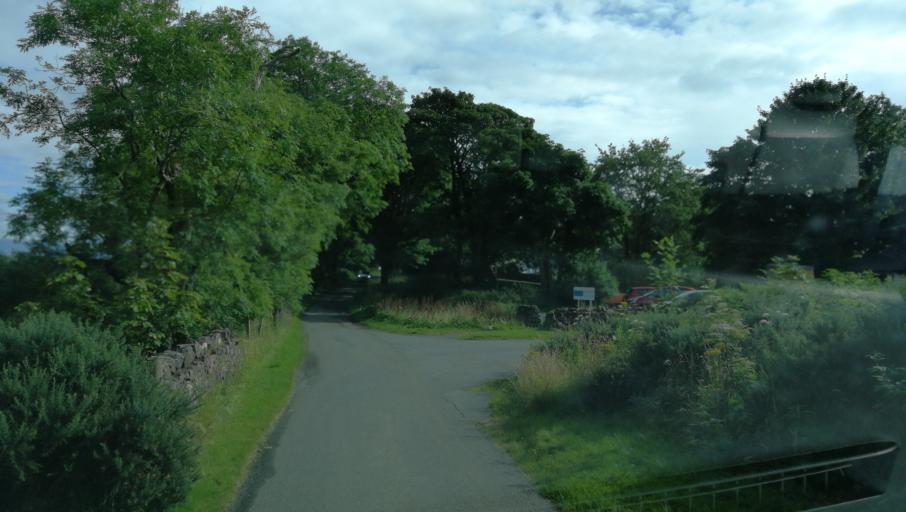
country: GB
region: Scotland
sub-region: Highland
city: Isle of Skye
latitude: 57.3972
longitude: -6.5677
